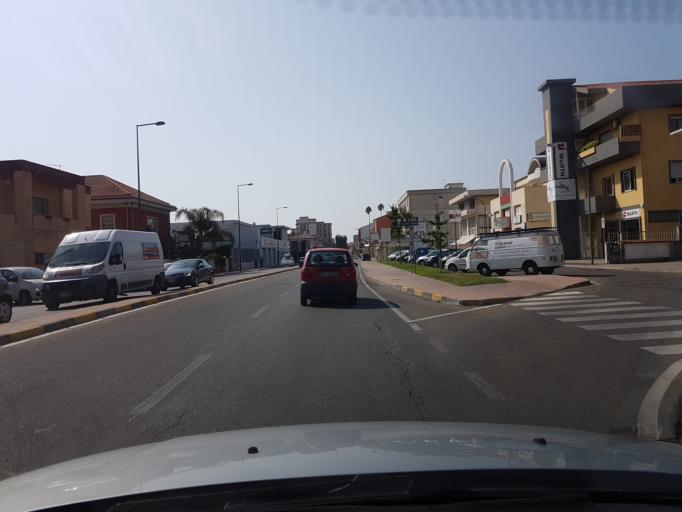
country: IT
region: Sardinia
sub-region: Provincia di Oristano
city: Oristano
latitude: 39.9119
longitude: 8.5874
